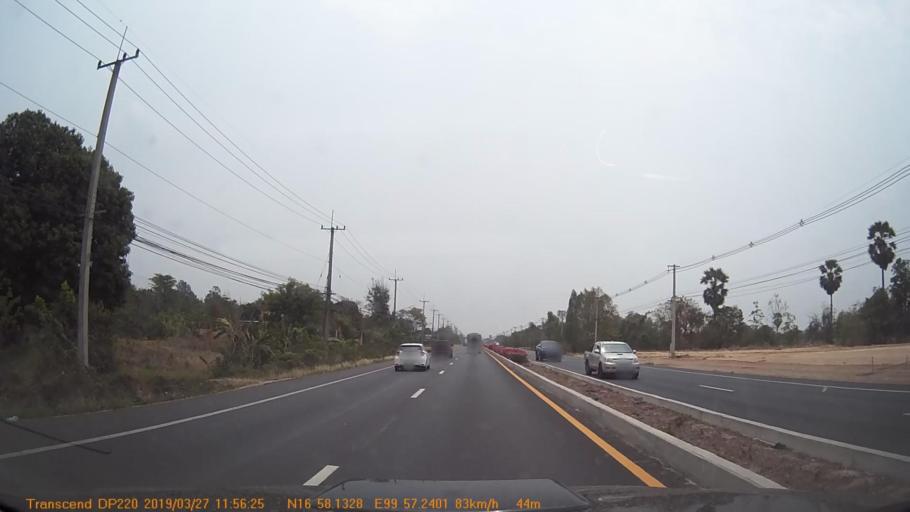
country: TH
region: Sukhothai
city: Kong Krailat
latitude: 16.9686
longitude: 99.9542
